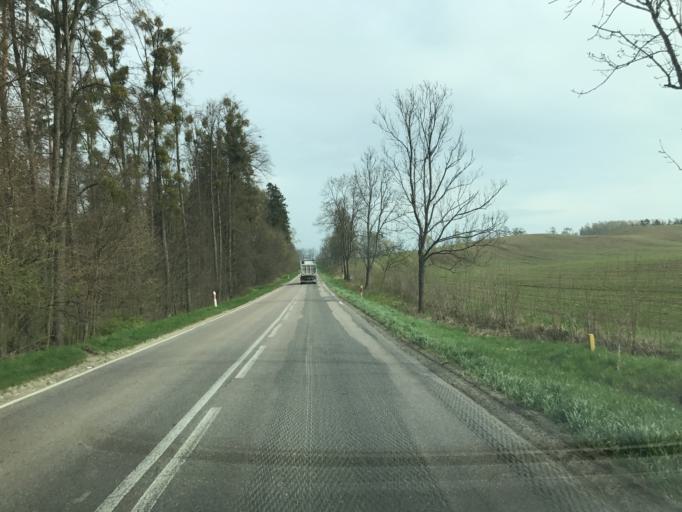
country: PL
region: Warmian-Masurian Voivodeship
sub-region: Powiat ostrodzki
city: Gierzwald
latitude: 53.5587
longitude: 20.0938
